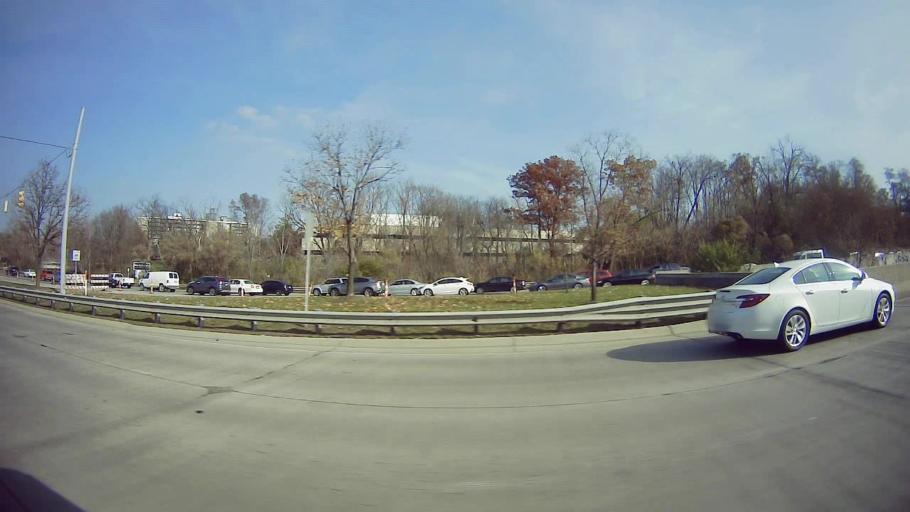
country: US
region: Michigan
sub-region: Oakland County
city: Bingham Farms
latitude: 42.4773
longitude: -83.2850
